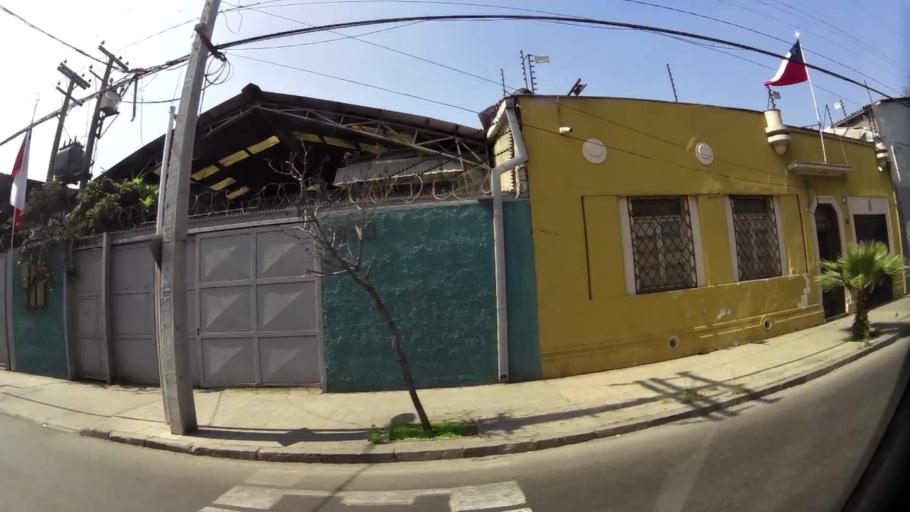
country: CL
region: Santiago Metropolitan
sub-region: Provincia de Santiago
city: Santiago
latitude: -33.4613
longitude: -70.6742
